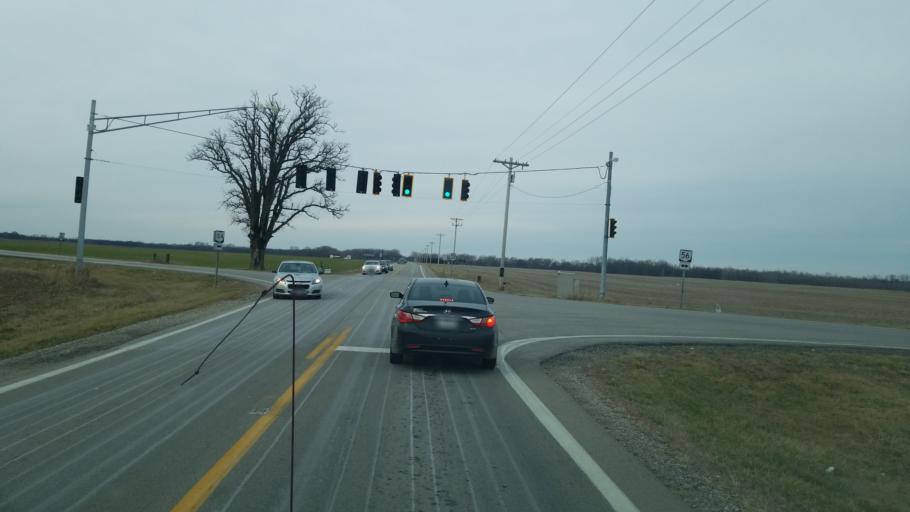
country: US
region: Ohio
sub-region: Pickaway County
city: Circleville
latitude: 39.6114
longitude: -83.0060
